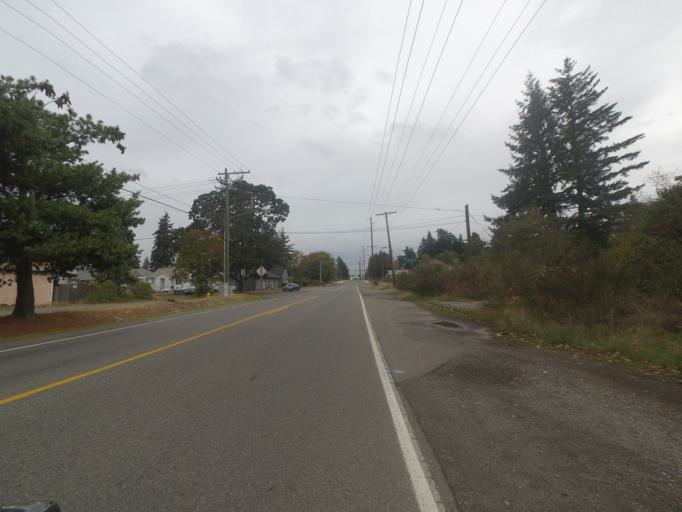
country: US
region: Washington
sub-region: Pierce County
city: McChord Air Force Base
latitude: 47.1564
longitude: -122.5000
